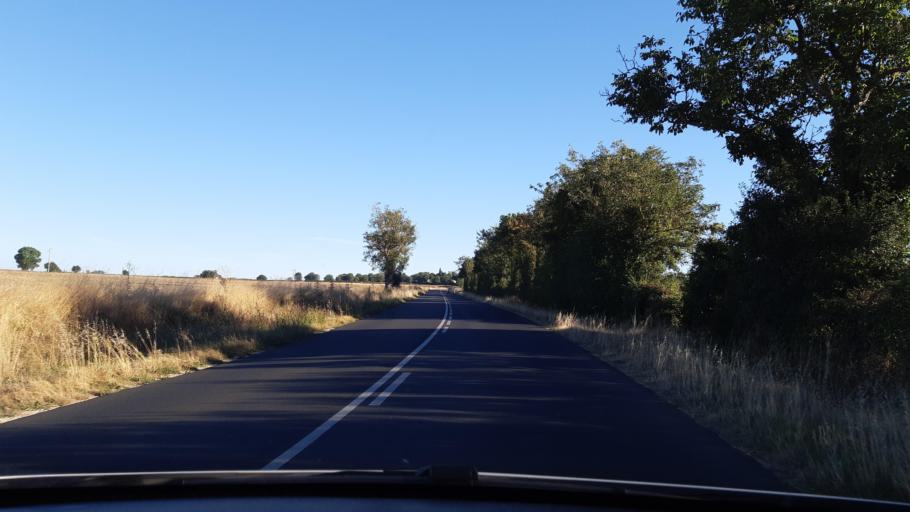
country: FR
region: Poitou-Charentes
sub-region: Departement des Deux-Sevres
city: Exireuil
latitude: 46.4306
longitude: -0.2028
